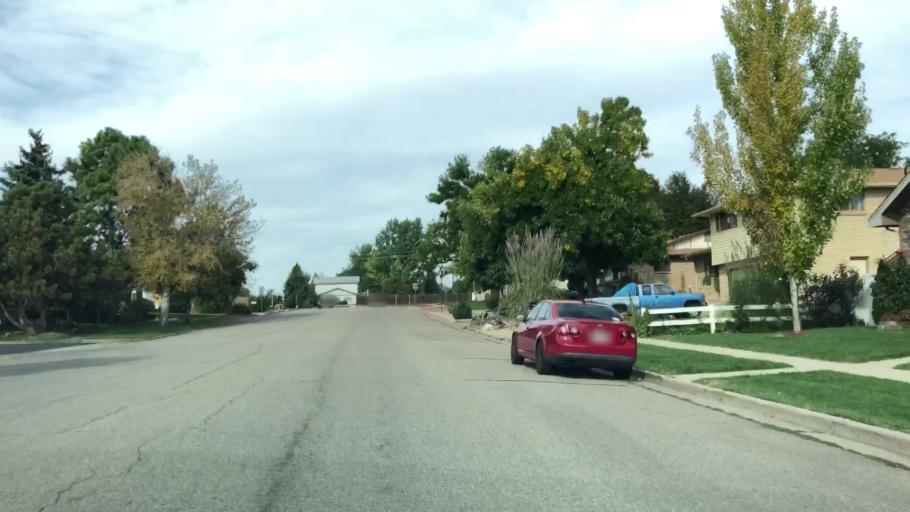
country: US
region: Colorado
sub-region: Larimer County
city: Loveland
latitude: 40.4127
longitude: -105.0571
